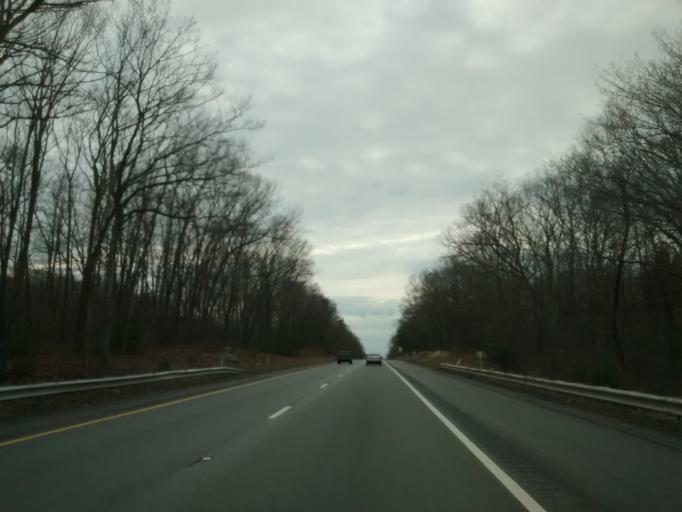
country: US
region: Massachusetts
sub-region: Worcester County
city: Whitinsville
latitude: 42.0707
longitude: -71.6724
